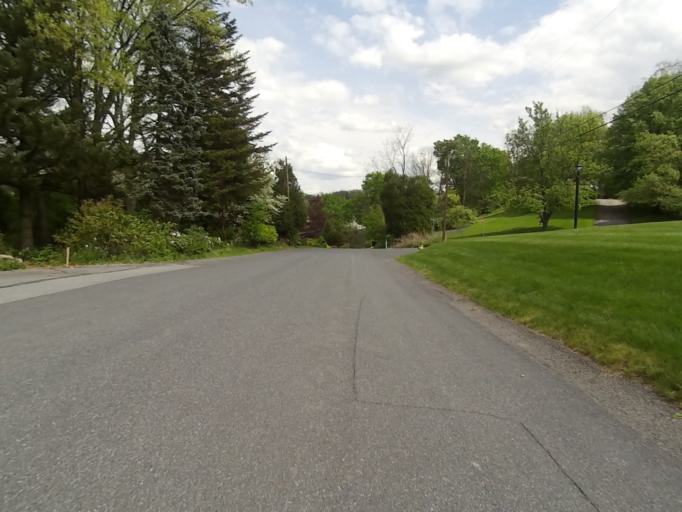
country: US
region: Pennsylvania
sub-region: Centre County
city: Houserville
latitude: 40.8111
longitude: -77.8396
